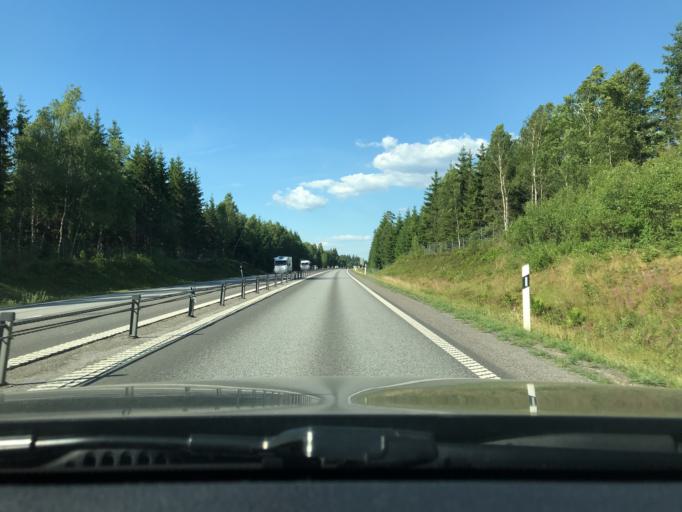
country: SE
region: Skane
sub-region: Osby Kommun
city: Osby
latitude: 56.4341
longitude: 14.0623
